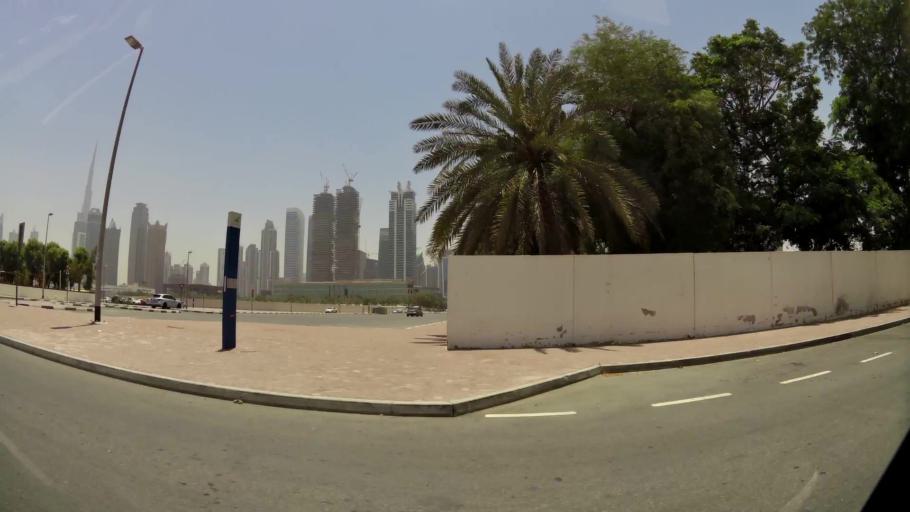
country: AE
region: Dubai
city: Dubai
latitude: 25.1907
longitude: 55.2522
